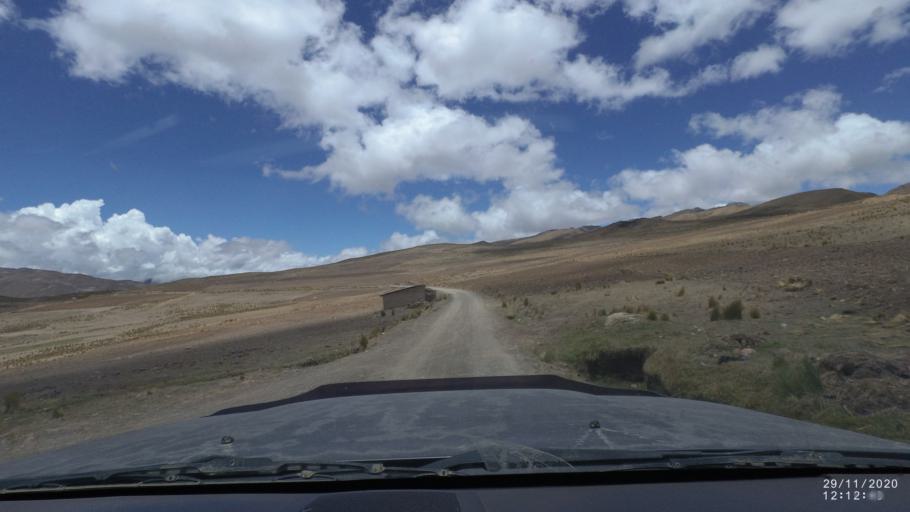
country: BO
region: Cochabamba
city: Cochabamba
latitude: -17.1115
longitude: -66.3030
